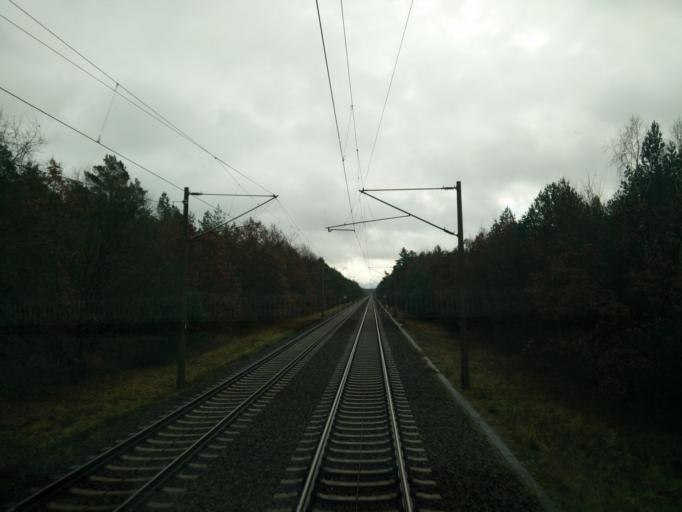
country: DE
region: Mecklenburg-Vorpommern
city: Grabow
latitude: 53.2952
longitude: 11.5433
